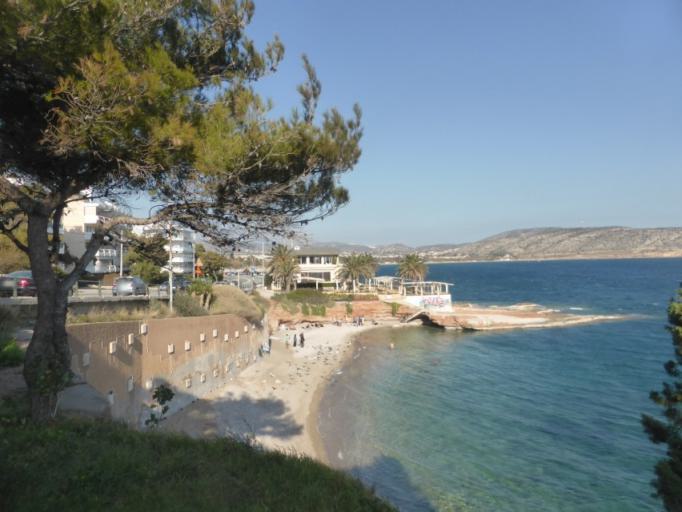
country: GR
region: Attica
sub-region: Nomarchia Anatolikis Attikis
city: Vari
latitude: 37.8115
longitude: 23.8006
